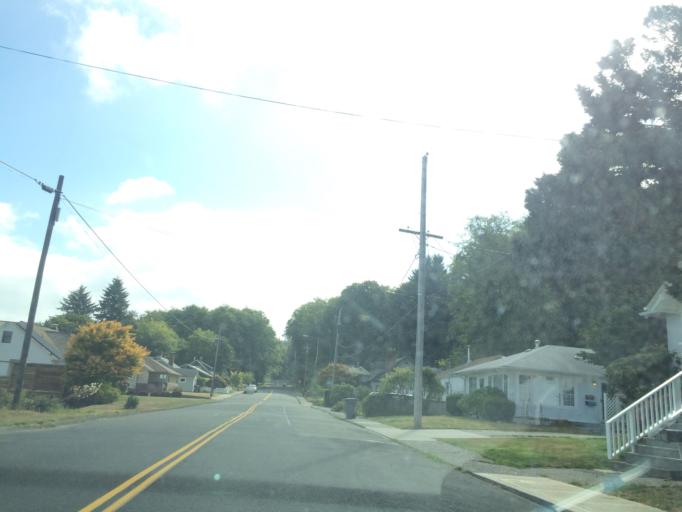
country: US
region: Oregon
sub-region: Clatsop County
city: Astoria
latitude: 46.1854
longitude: -123.8206
